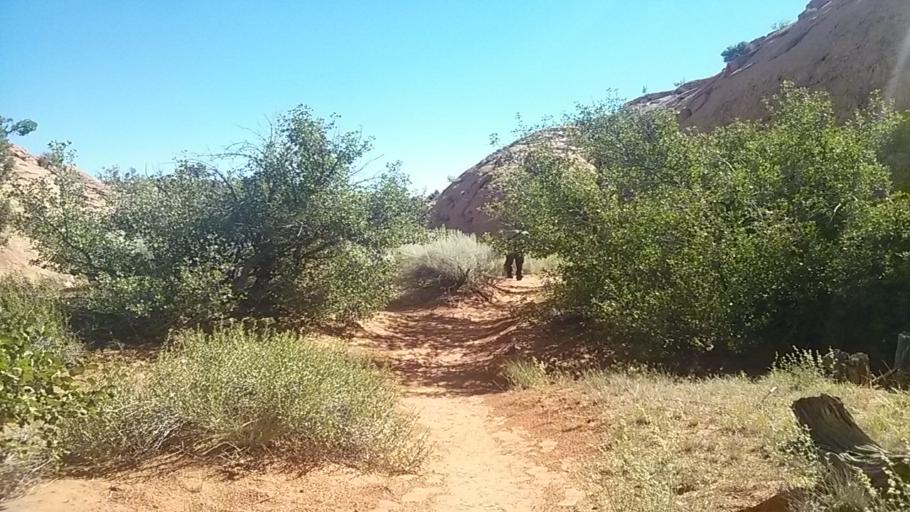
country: US
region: Arizona
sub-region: Coconino County
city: Page
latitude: 37.4804
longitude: -111.2184
